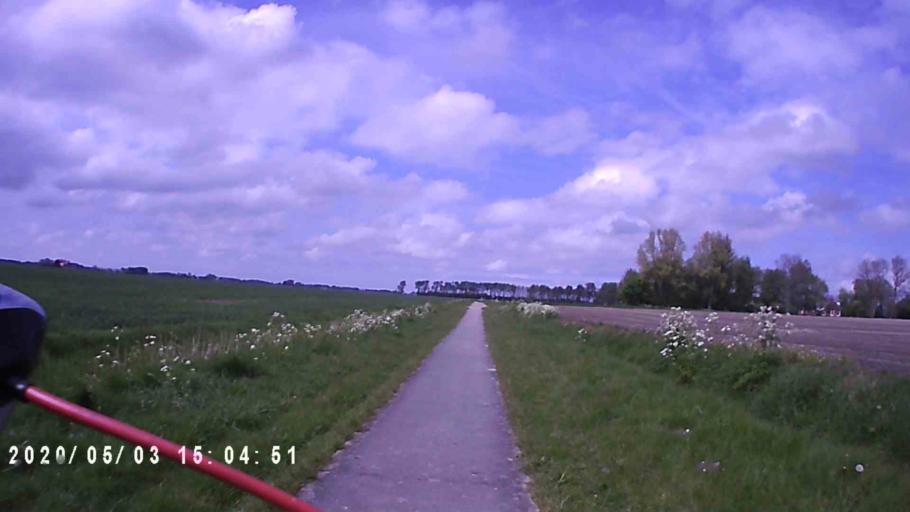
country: NL
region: Groningen
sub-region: Gemeente Zuidhorn
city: Oldehove
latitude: 53.3692
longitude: 6.4421
